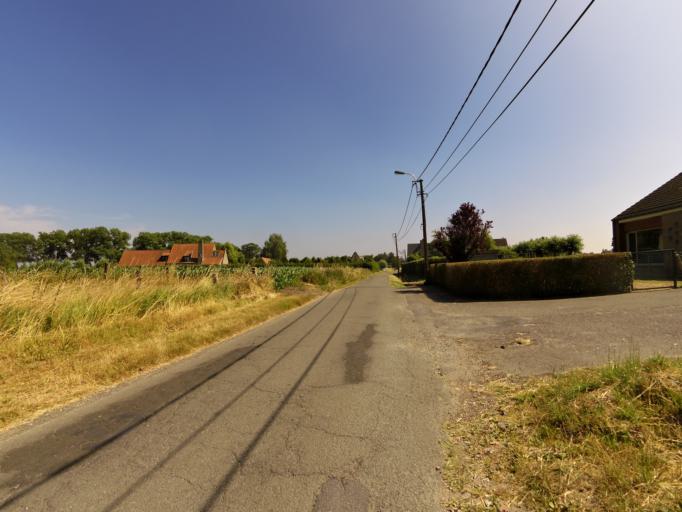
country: BE
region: Flanders
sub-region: Provincie West-Vlaanderen
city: Zedelgem
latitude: 51.1487
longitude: 3.1413
